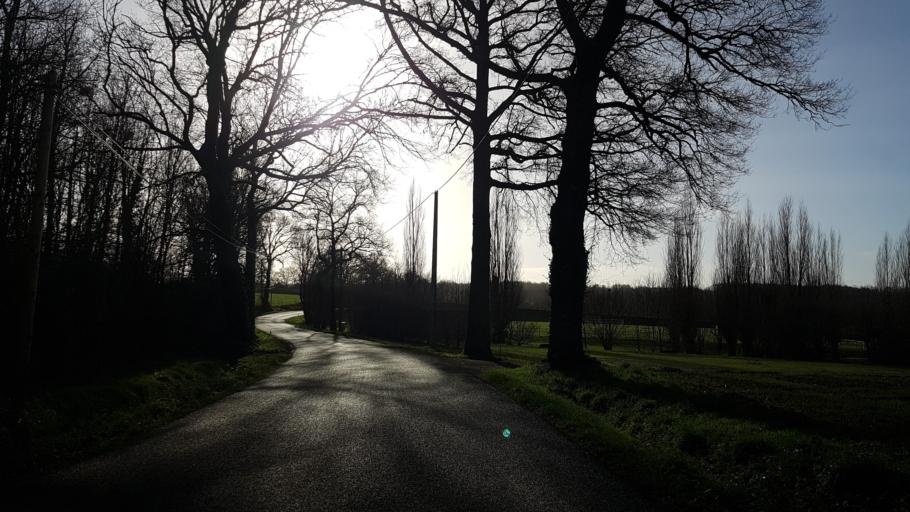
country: FR
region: Poitou-Charentes
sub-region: Departement de la Charente
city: Etagnac
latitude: 45.9457
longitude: 0.7860
